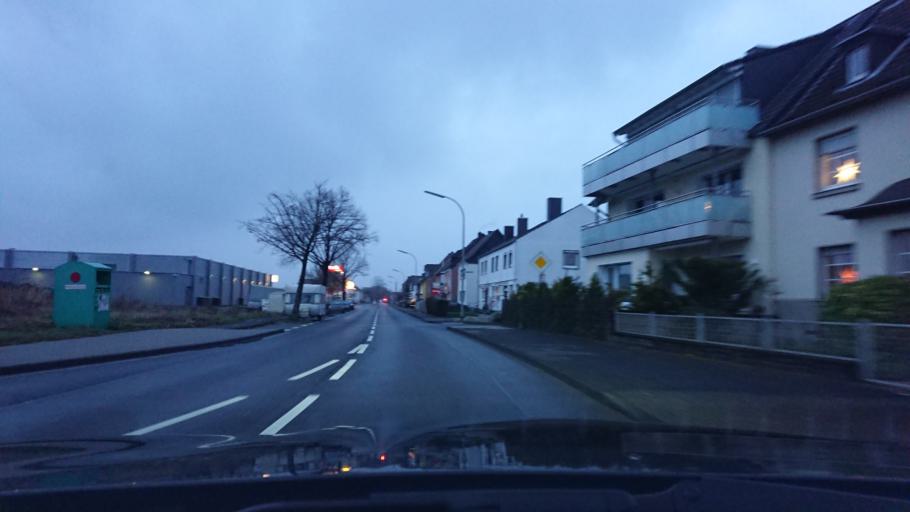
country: DE
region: North Rhine-Westphalia
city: Niederkassel
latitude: 50.8288
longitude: 7.0317
